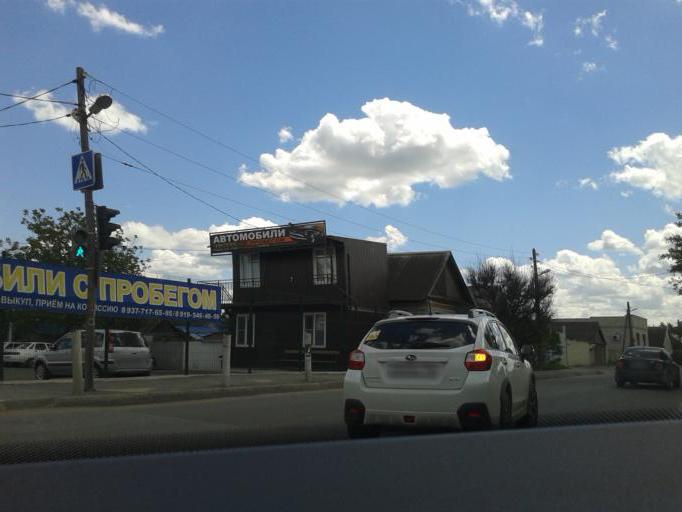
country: RU
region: Volgograd
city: Volgograd
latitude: 48.7040
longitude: 44.4493
